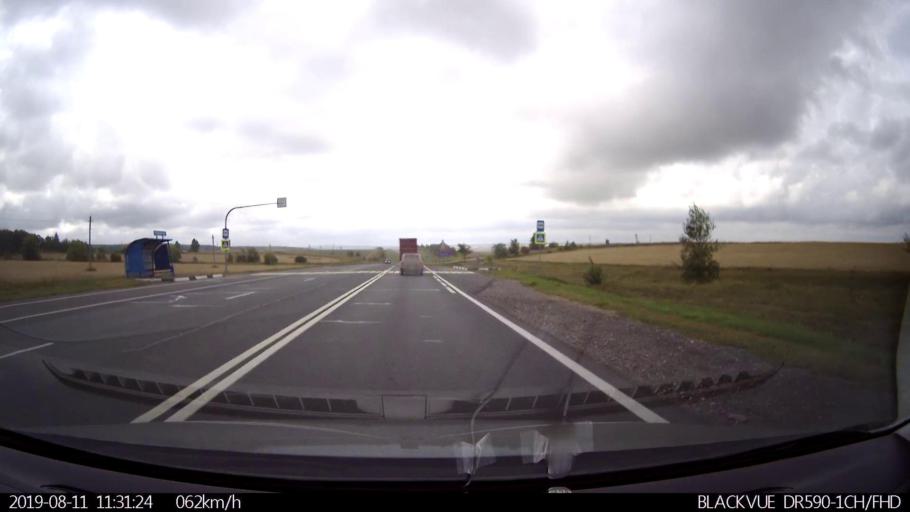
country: RU
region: Ulyanovsk
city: Krasnyy Gulyay
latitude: 54.0479
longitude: 48.2160
